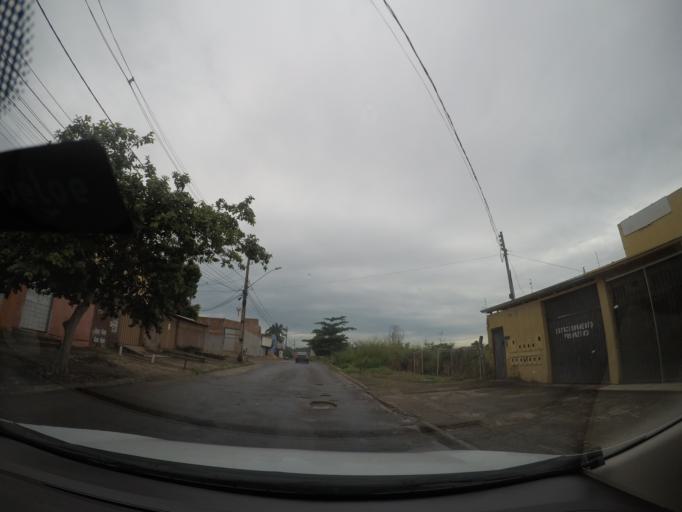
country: BR
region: Goias
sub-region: Goiania
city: Goiania
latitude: -16.6483
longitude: -49.2631
